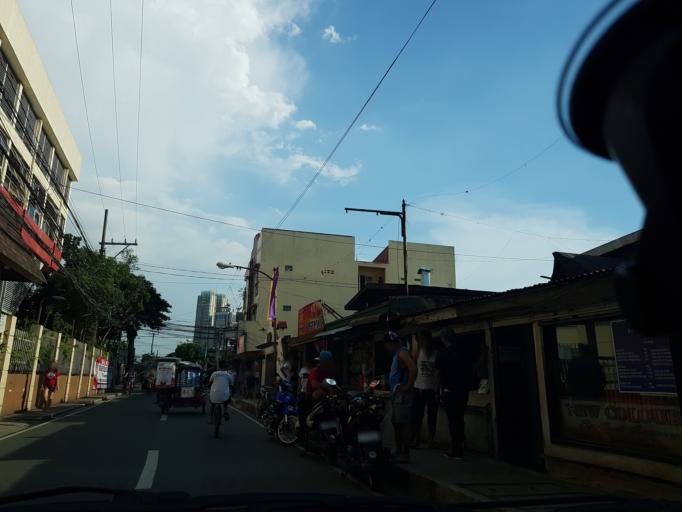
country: PH
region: Metro Manila
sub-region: Marikina
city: Calumpang
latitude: 14.6168
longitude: 121.0815
